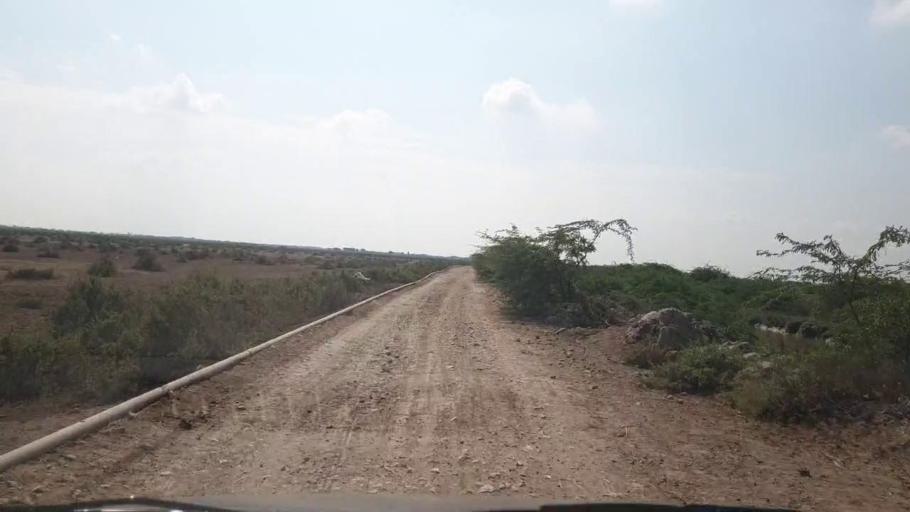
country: PK
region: Sindh
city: Badin
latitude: 24.5045
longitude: 68.6081
